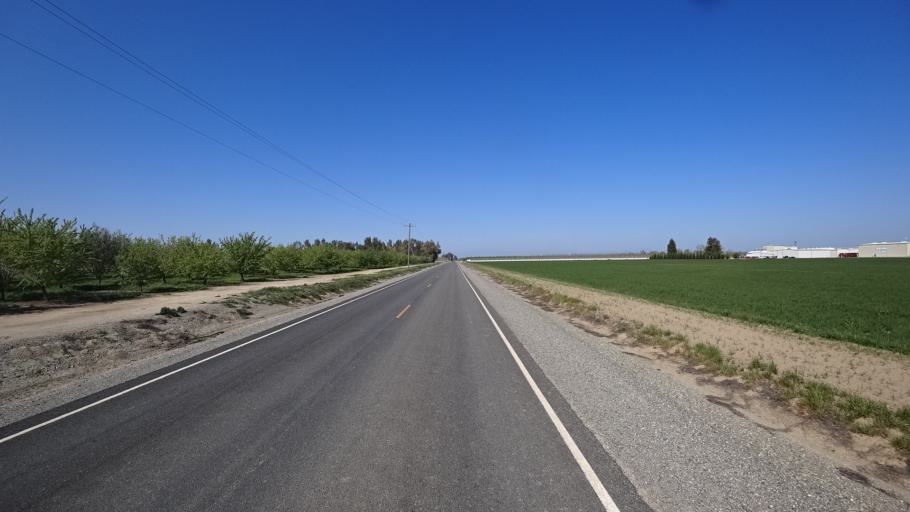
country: US
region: California
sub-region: Glenn County
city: Hamilton City
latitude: 39.6597
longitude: -122.0514
